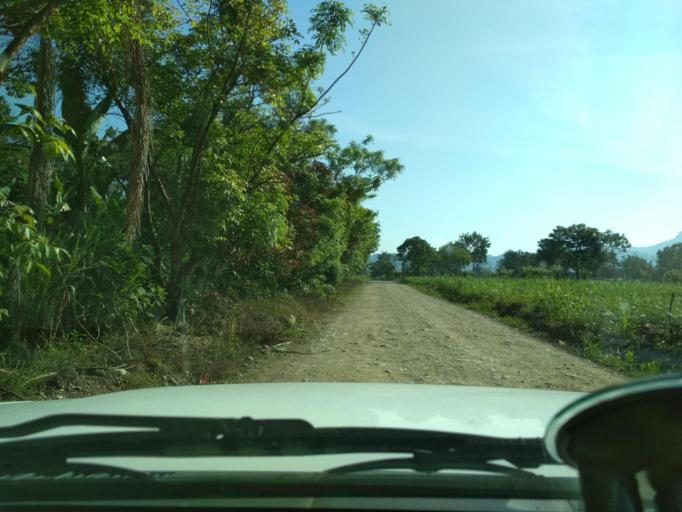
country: MX
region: Veracruz
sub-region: Chocaman
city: San Jose Neria
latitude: 18.9935
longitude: -97.0030
